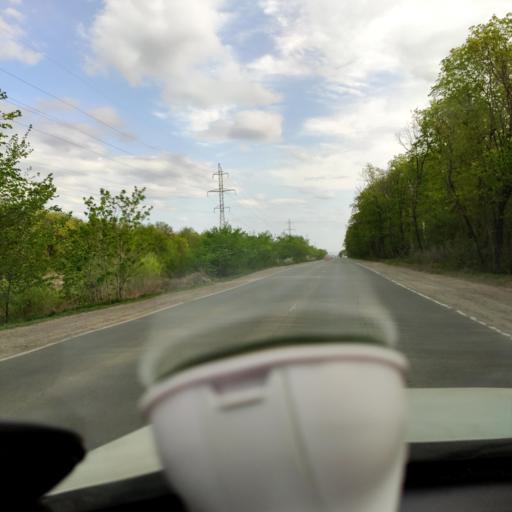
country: RU
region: Samara
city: Novosemeykino
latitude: 53.3375
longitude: 50.2510
